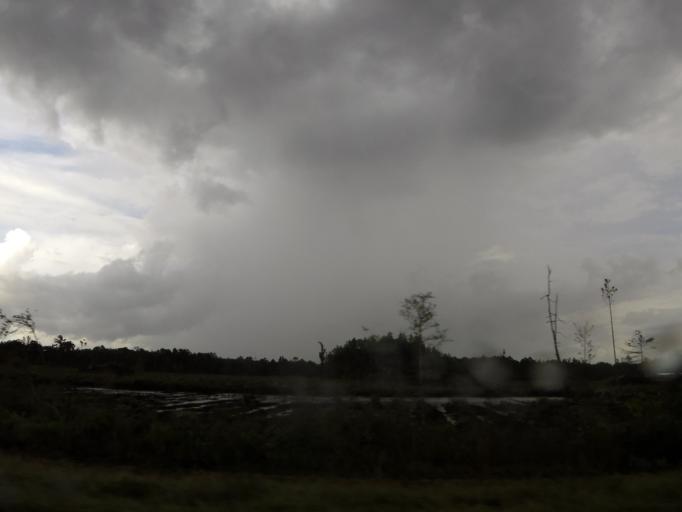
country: US
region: Florida
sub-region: Nassau County
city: Hilliard
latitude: 30.5483
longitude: -82.0409
